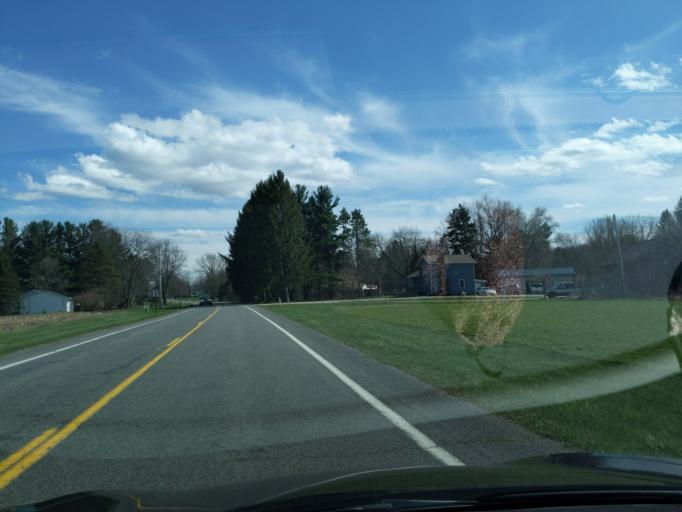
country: US
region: Michigan
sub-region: Ingham County
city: Mason
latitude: 42.5610
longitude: -84.4086
